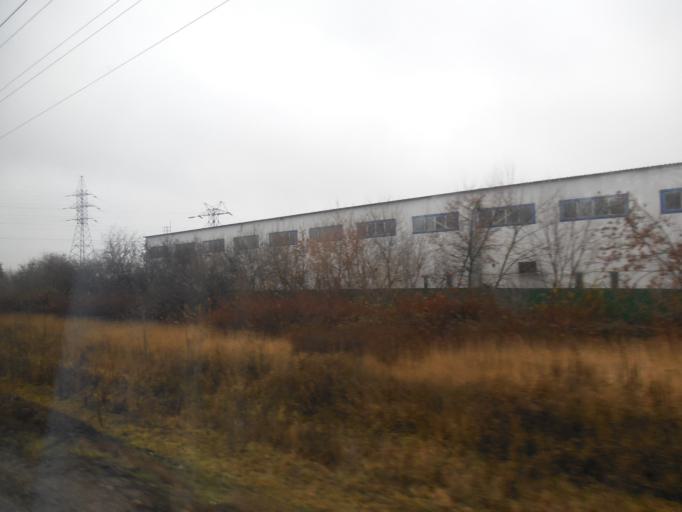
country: RU
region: Moskovskaya
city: Yam
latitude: 55.4876
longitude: 37.7333
